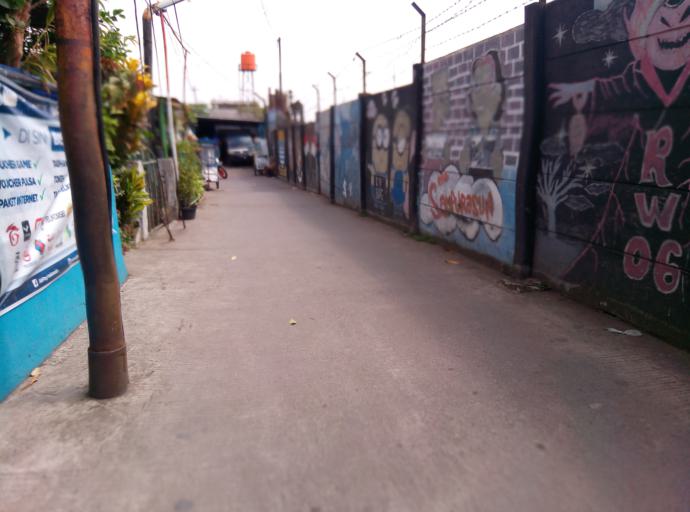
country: ID
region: West Java
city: Bandung
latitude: -6.9259
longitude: 107.6485
